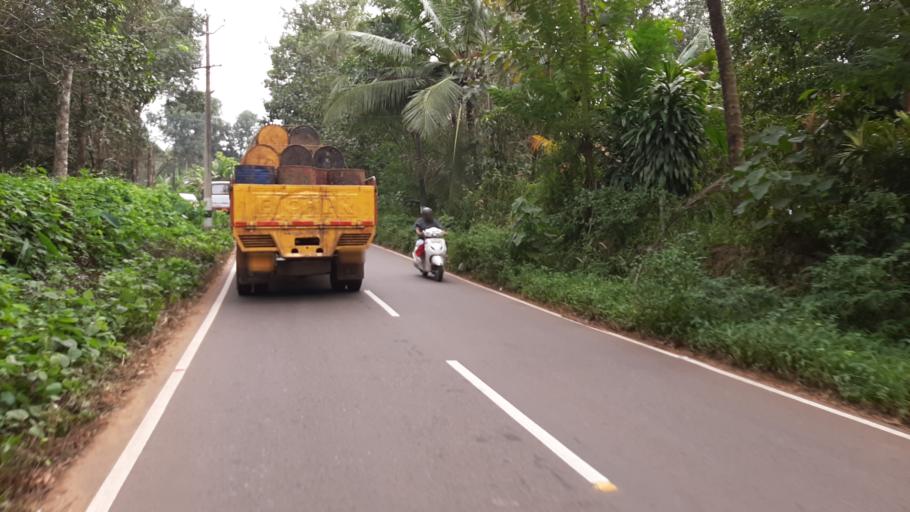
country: IN
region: Kerala
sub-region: Pattanamtitta
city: Pathanamthitta
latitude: 9.4678
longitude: 76.8701
